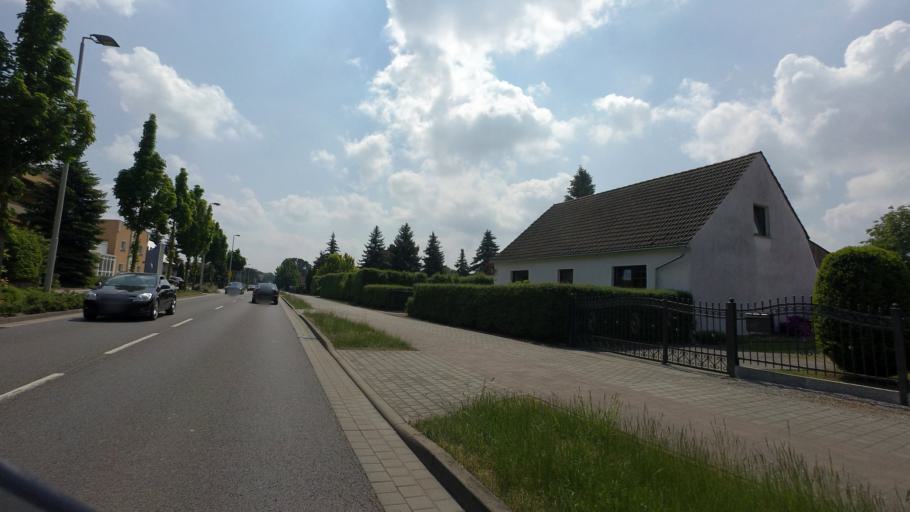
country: DE
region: Brandenburg
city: Cottbus
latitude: 51.7138
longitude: 14.3528
